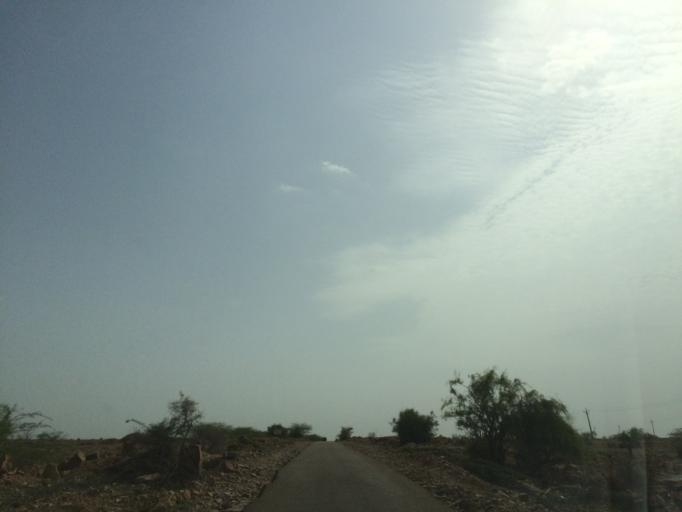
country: IN
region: Rajasthan
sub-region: Jaisalmer
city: Jaisalmer
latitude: 26.8854
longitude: 70.9130
